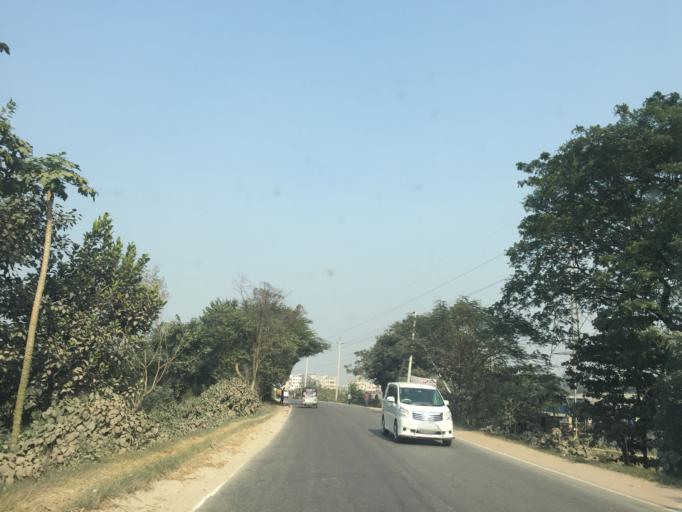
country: BD
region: Dhaka
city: Tungi
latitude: 23.8244
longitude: 90.3433
